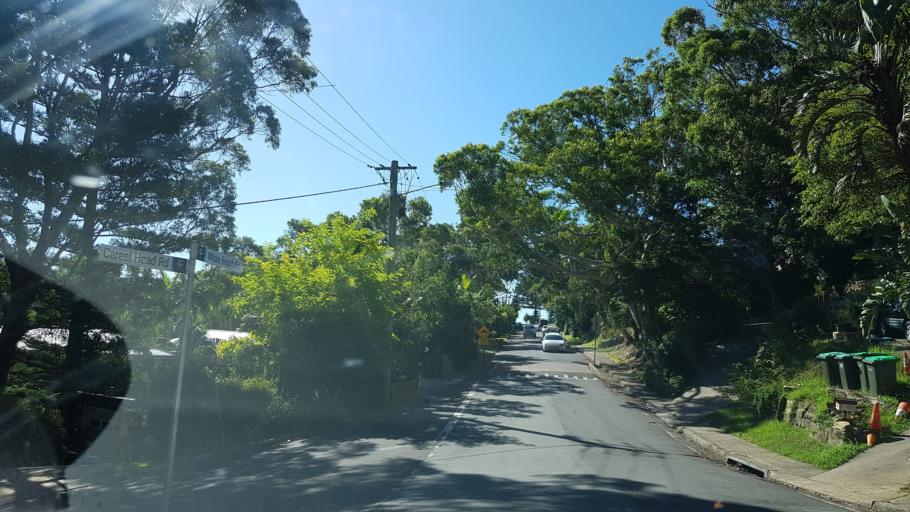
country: AU
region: New South Wales
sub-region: Pittwater
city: Palm Beach
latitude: -33.6192
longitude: 151.3373
